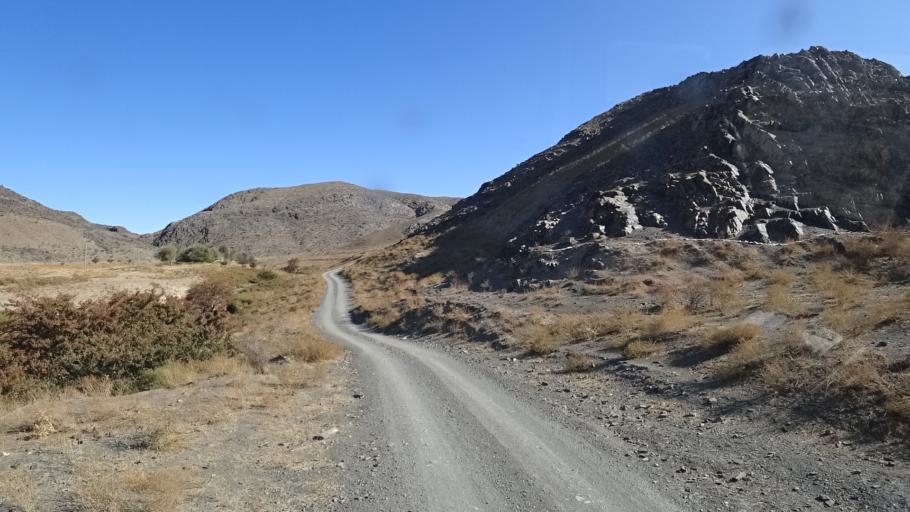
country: UZ
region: Navoiy
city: Nurota
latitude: 40.2999
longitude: 65.6134
